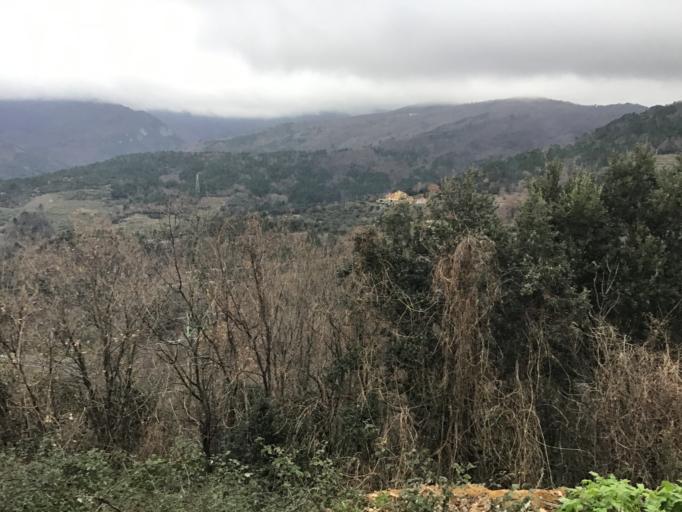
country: IT
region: Liguria
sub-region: Provincia di Savona
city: Orco Feglino
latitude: 44.2213
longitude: 8.3378
